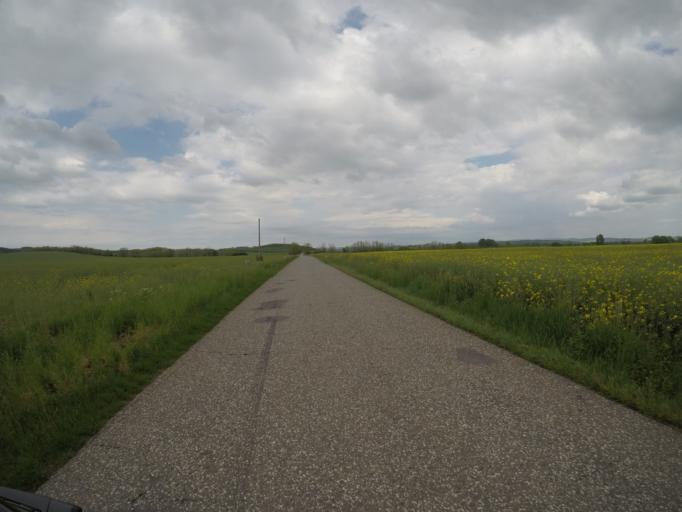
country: SK
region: Nitriansky
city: Sahy
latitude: 48.0728
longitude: 18.8609
